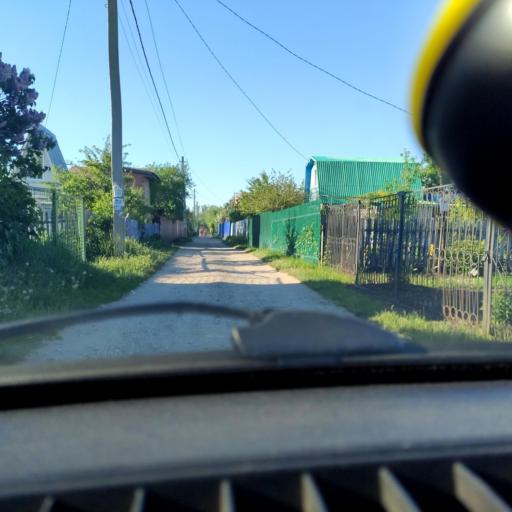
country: RU
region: Samara
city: Tol'yatti
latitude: 53.5947
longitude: 49.3147
